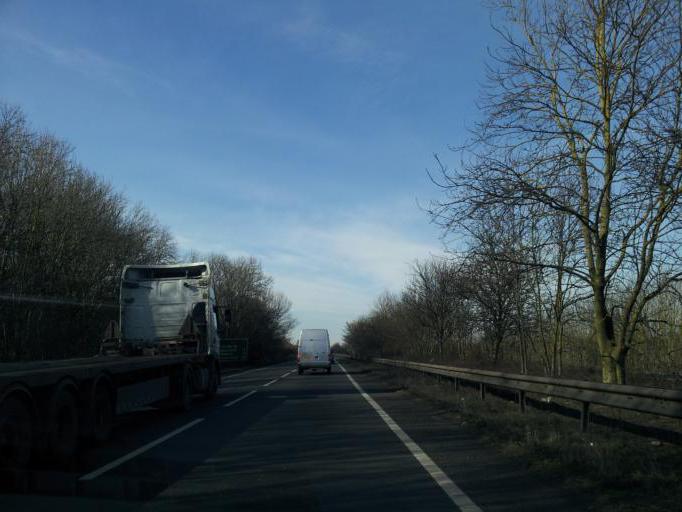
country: GB
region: England
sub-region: District of Rutland
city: Tickencote
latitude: 52.6932
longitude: -0.5652
